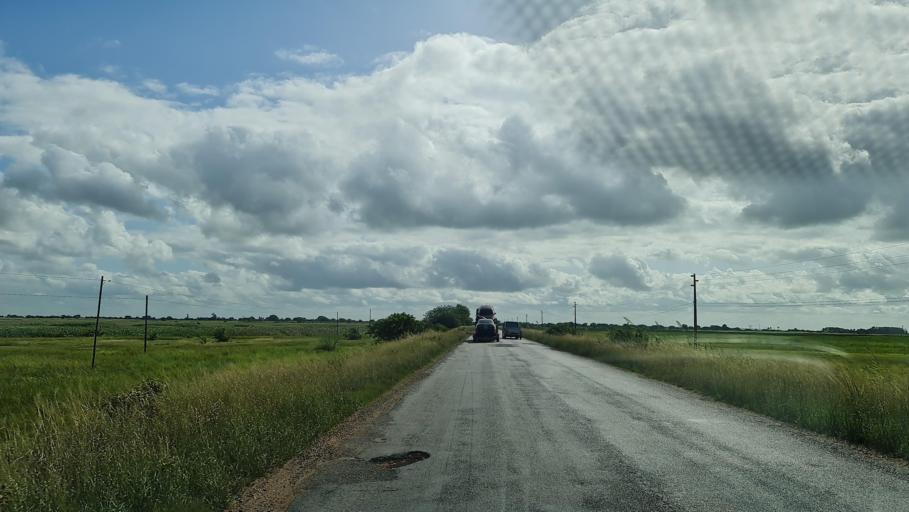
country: MZ
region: Gaza
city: Macia
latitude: -25.0974
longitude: 32.8286
